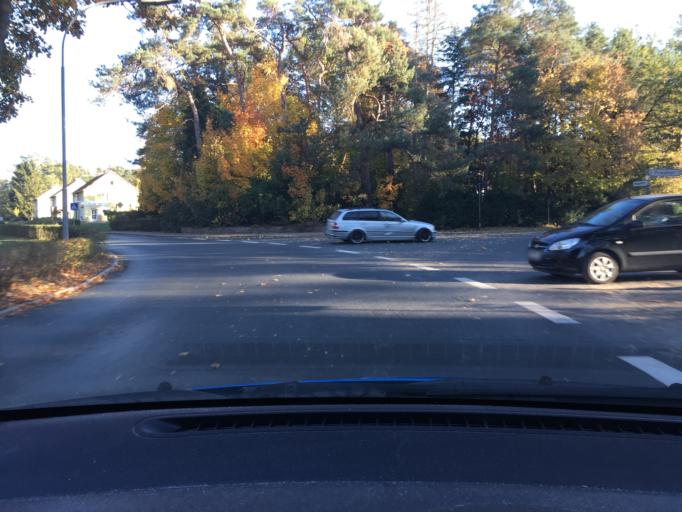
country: DE
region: Lower Saxony
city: Tosterglope
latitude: 53.2664
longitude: 10.7920
